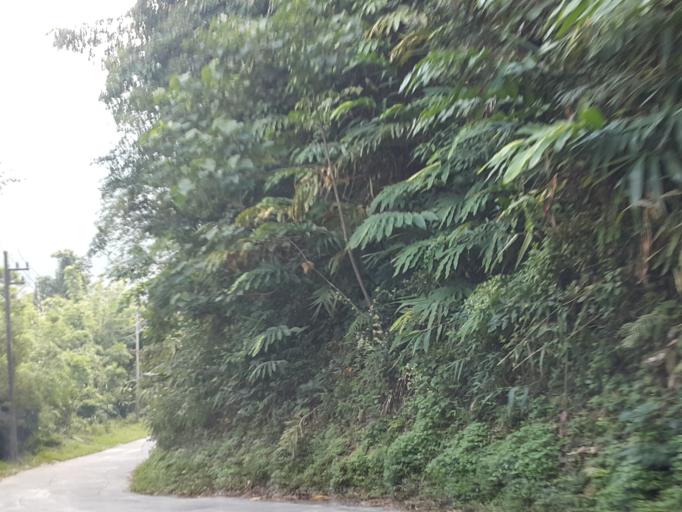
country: TH
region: Chiang Mai
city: Mae On
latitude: 18.8883
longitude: 99.3571
